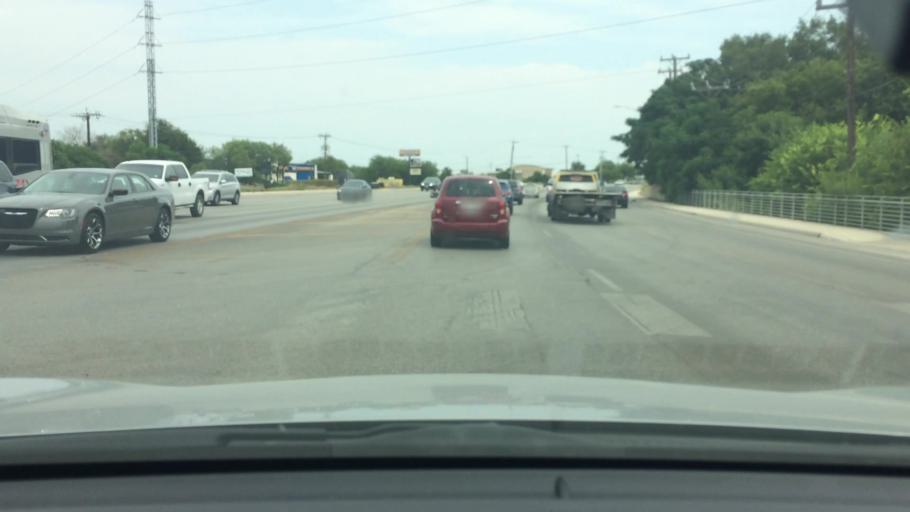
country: US
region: Texas
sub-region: Bexar County
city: Leon Valley
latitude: 29.4746
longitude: -98.6548
